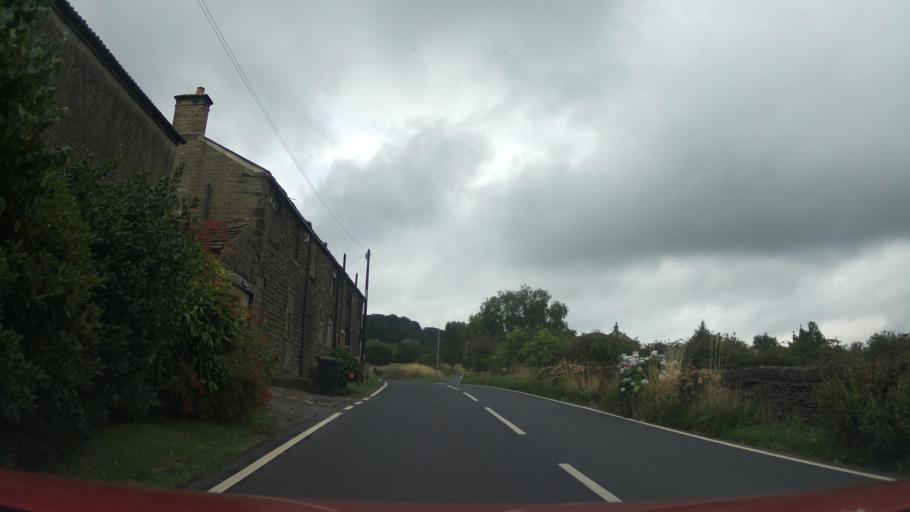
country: GB
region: England
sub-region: Kirklees
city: Shelley
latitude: 53.5806
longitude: -1.6920
